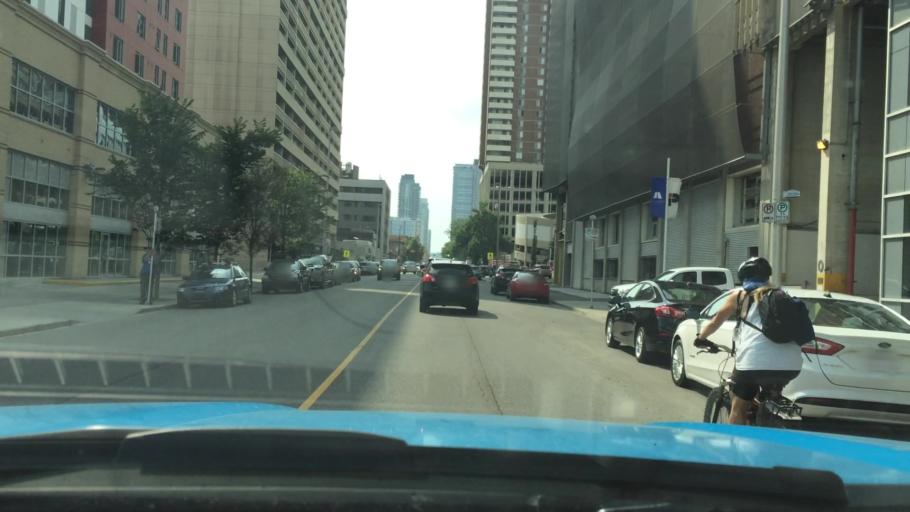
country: CA
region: Alberta
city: Calgary
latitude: 51.0433
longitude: -114.0620
